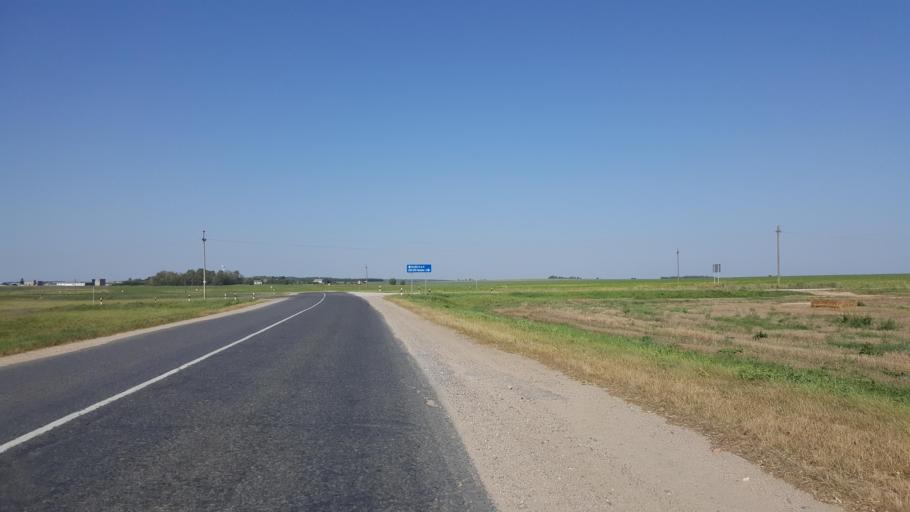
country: BY
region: Brest
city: Kamyanyets
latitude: 52.4174
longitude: 23.6205
